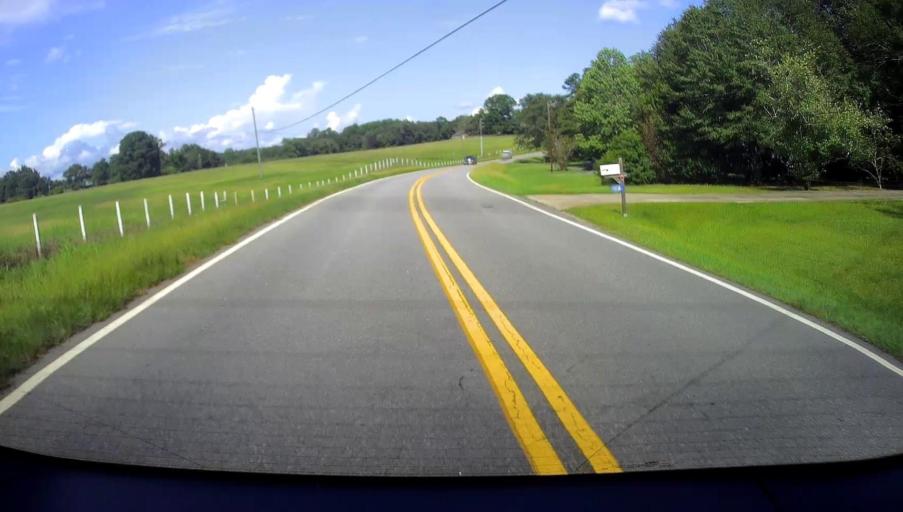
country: US
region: Georgia
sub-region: Upson County
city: Hannahs Mill
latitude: 32.9508
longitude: -84.3208
